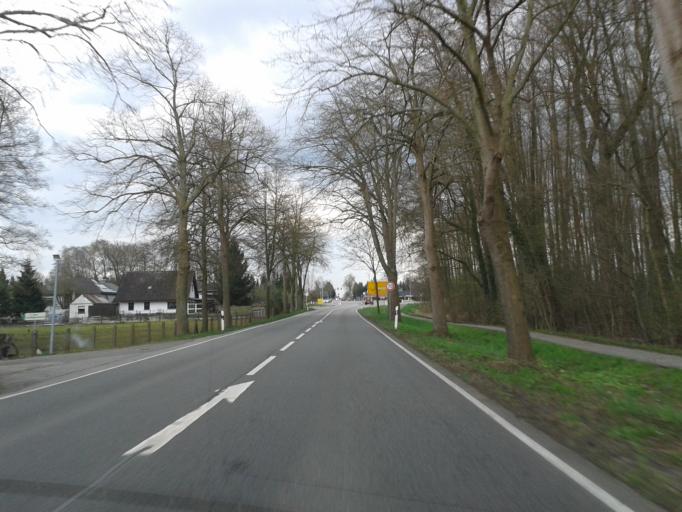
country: DE
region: Saxony-Anhalt
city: Salzwedel
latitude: 52.8621
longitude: 11.1141
